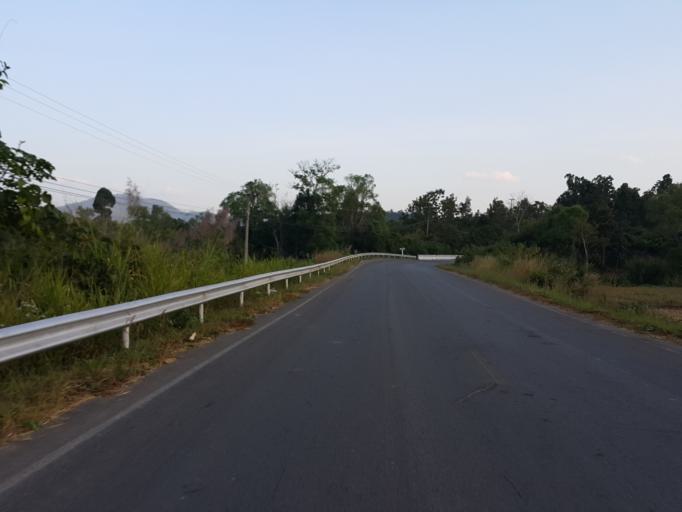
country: TH
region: Lamphun
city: Thung Hua Chang
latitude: 17.9305
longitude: 99.0493
